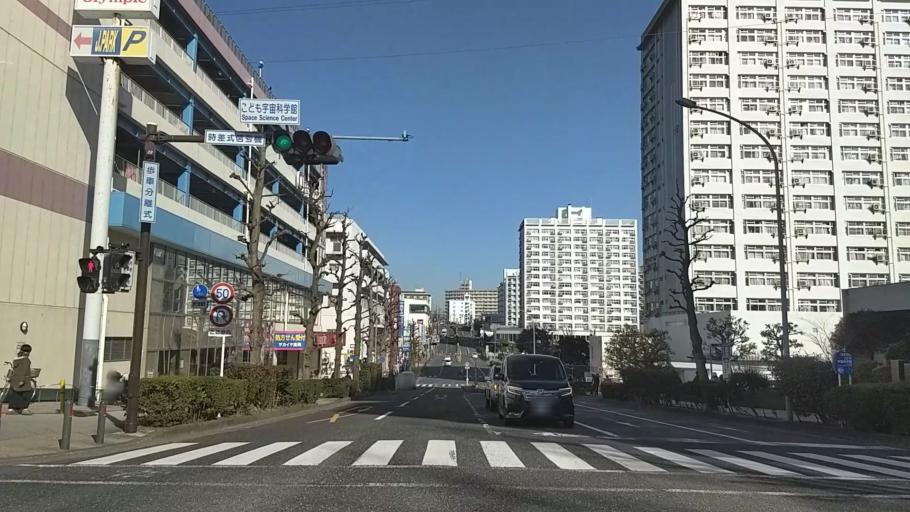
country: JP
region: Kanagawa
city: Kamakura
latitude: 35.3770
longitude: 139.5963
